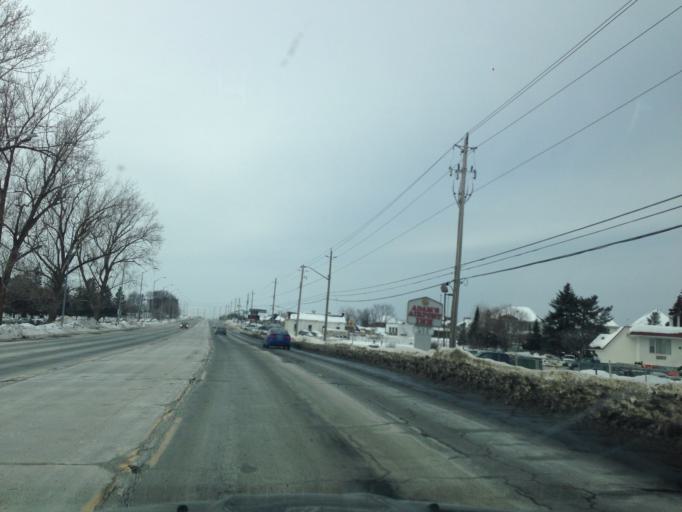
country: CA
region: Ontario
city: Ottawa
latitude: 45.3516
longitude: -75.6325
